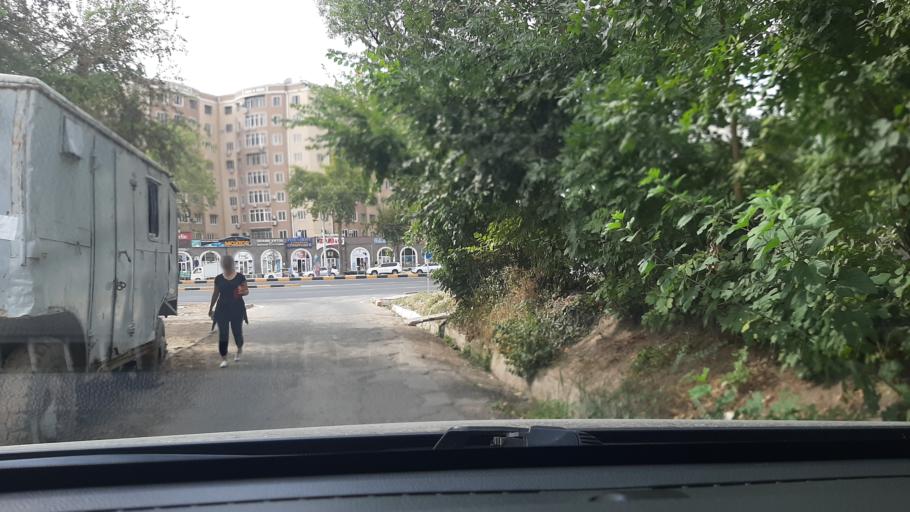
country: TJ
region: Dushanbe
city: Dushanbe
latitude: 38.5849
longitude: 68.7522
